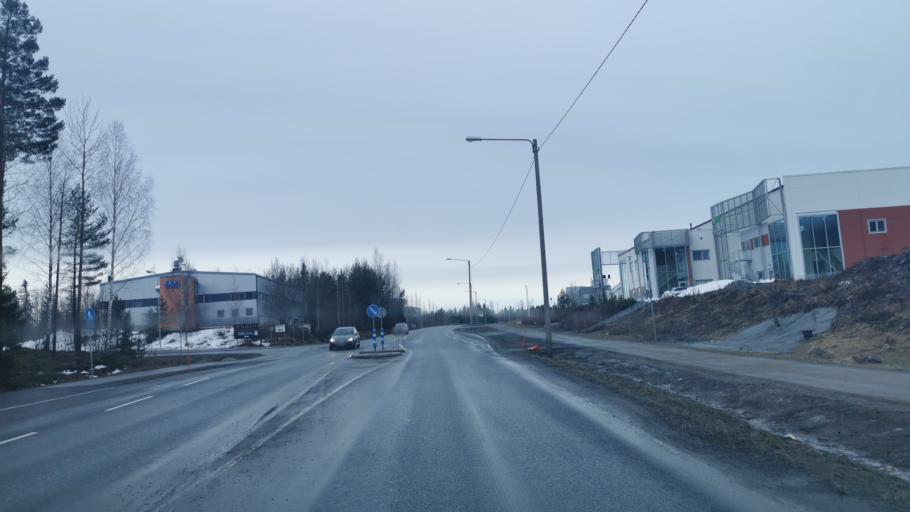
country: FI
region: Pirkanmaa
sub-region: Tampere
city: Pirkkala
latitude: 61.4352
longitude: 23.6288
